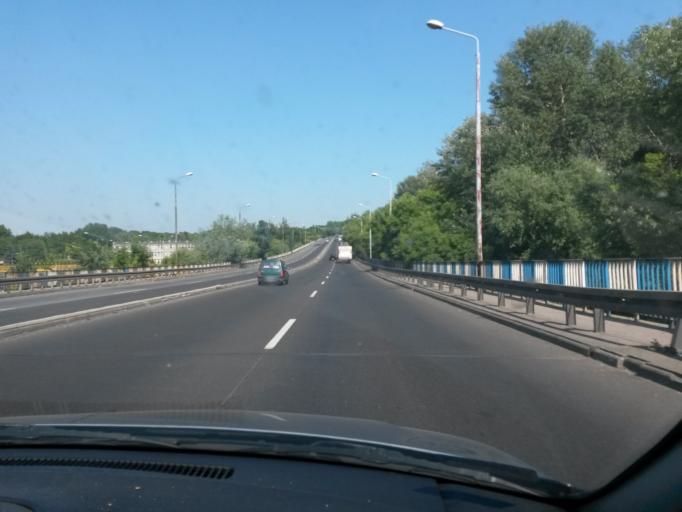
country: PL
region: Silesian Voivodeship
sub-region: Powiat bedzinski
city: Bedzin
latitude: 50.3009
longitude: 19.1403
